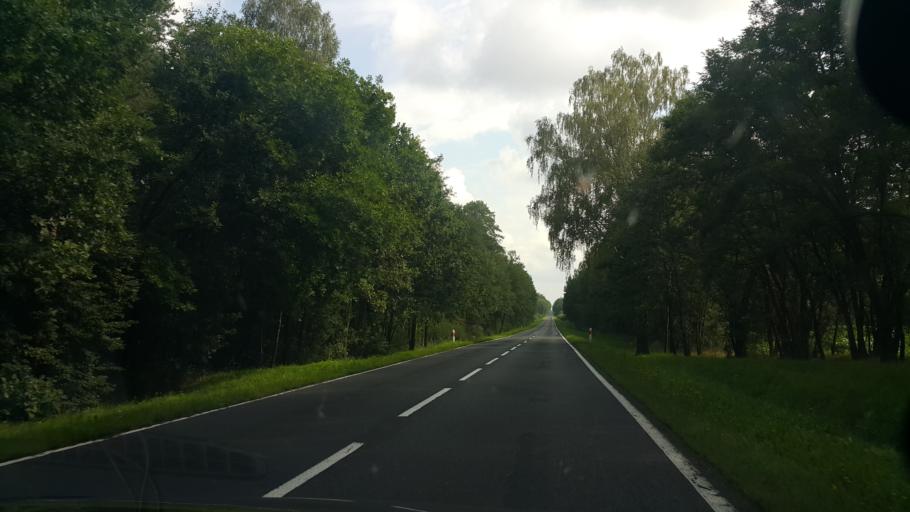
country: PL
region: Lublin Voivodeship
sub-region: Powiat wlodawski
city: Hansk
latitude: 51.4832
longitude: 23.3429
